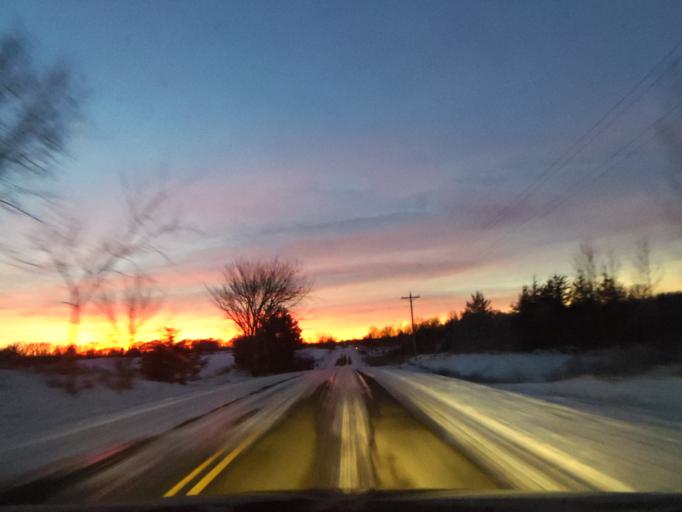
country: US
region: Minnesota
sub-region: Chisago County
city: Center City
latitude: 45.3542
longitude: -92.8040
